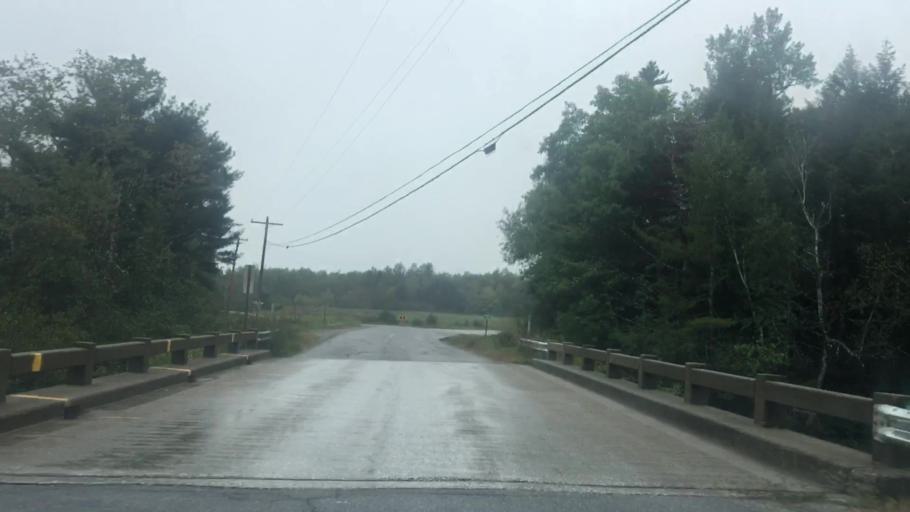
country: US
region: Maine
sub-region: Waldo County
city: Frankfort
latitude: 44.5495
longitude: -68.8731
